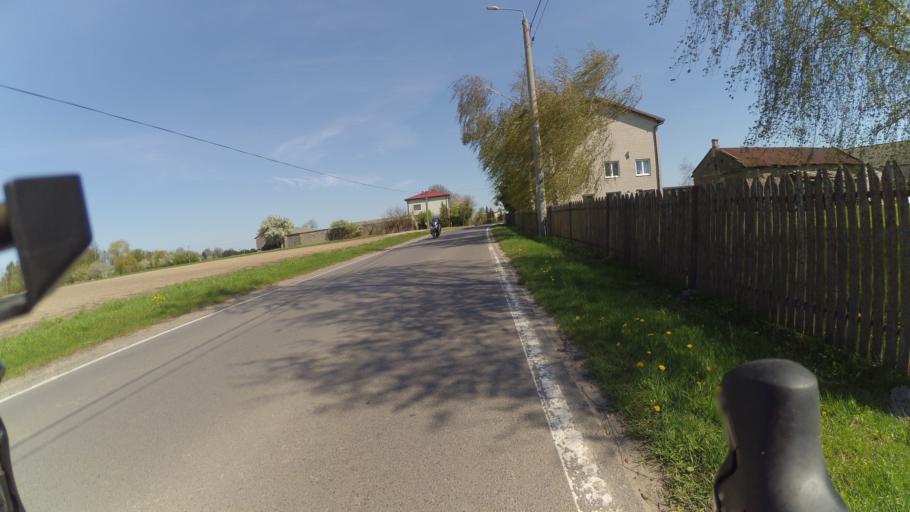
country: PL
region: Masovian Voivodeship
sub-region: Powiat warszawski zachodni
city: Leszno
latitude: 52.2449
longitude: 20.5445
